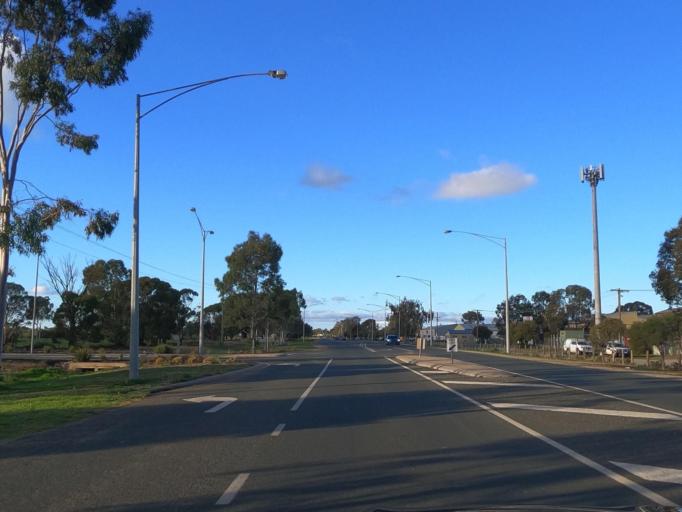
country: AU
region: Victoria
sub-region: Swan Hill
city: Swan Hill
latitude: -35.3423
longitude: 143.5335
